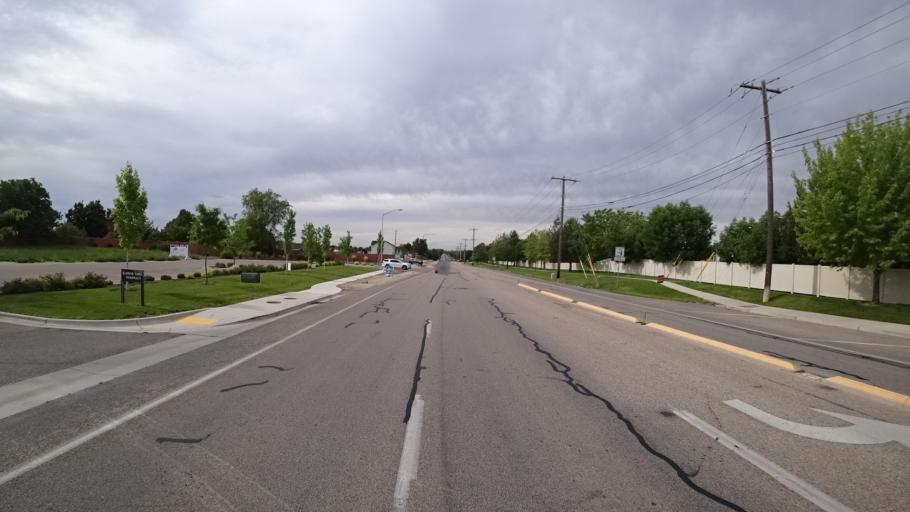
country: US
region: Idaho
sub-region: Ada County
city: Meridian
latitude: 43.5750
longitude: -116.3544
